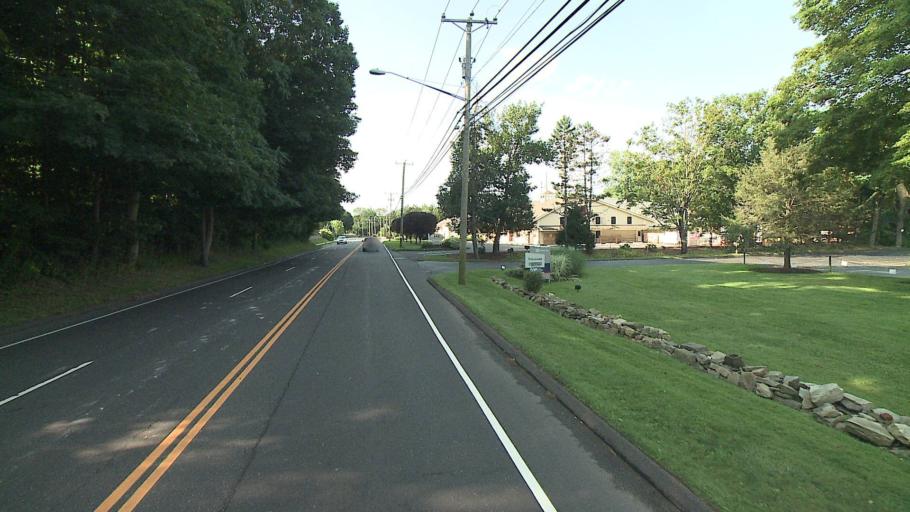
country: US
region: Connecticut
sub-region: Fairfield County
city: Wilton
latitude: 41.1785
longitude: -73.4162
